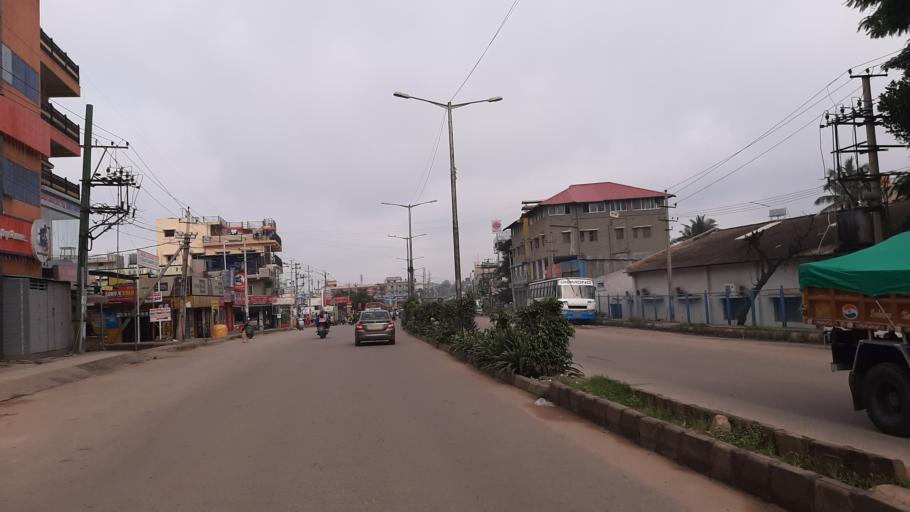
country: IN
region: Karnataka
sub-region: Bangalore Urban
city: Bangalore
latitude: 12.9857
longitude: 77.4791
